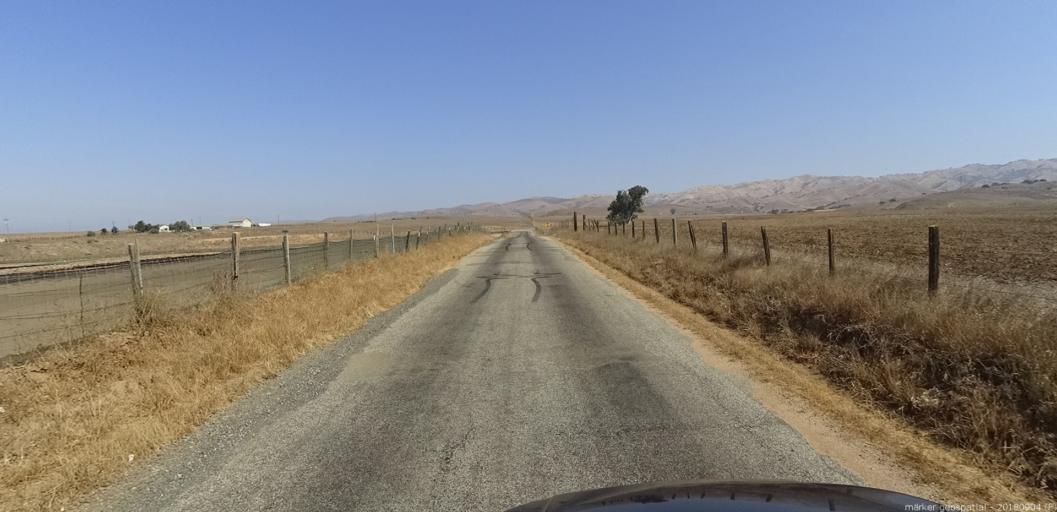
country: US
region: California
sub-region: Monterey County
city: Gonzales
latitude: 36.5081
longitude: -121.3649
